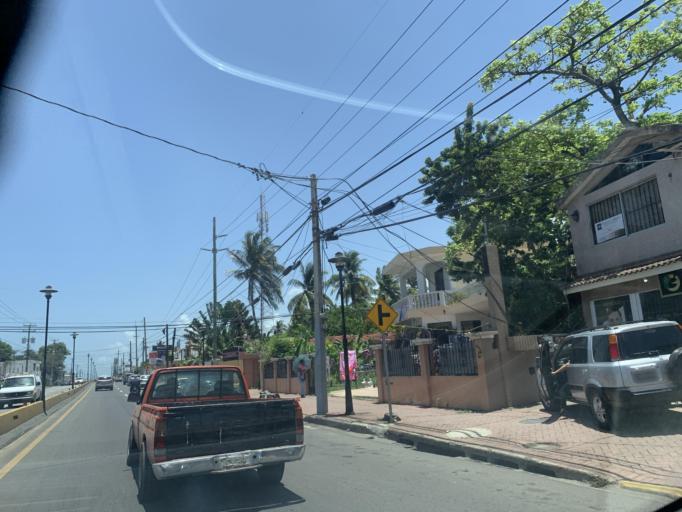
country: DO
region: Puerto Plata
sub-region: Puerto Plata
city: Puerto Plata
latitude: 19.7851
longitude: -70.6844
